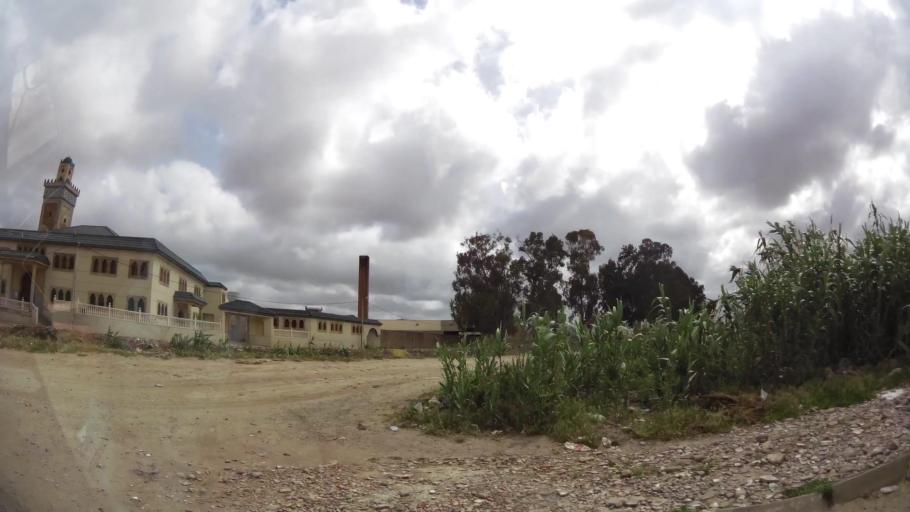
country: MA
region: Oriental
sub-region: Nador
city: Nador
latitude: 35.1574
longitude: -2.9381
